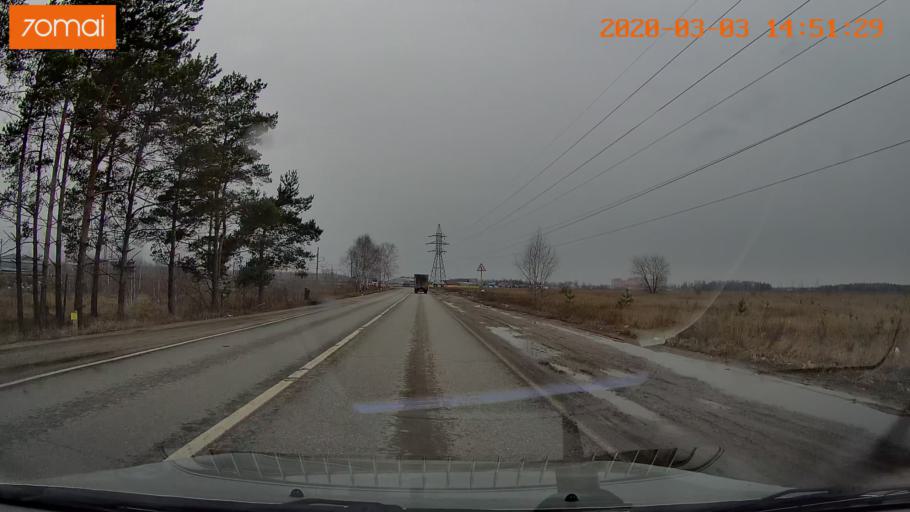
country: RU
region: Moskovskaya
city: Malakhovka
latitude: 55.6662
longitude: 38.0279
